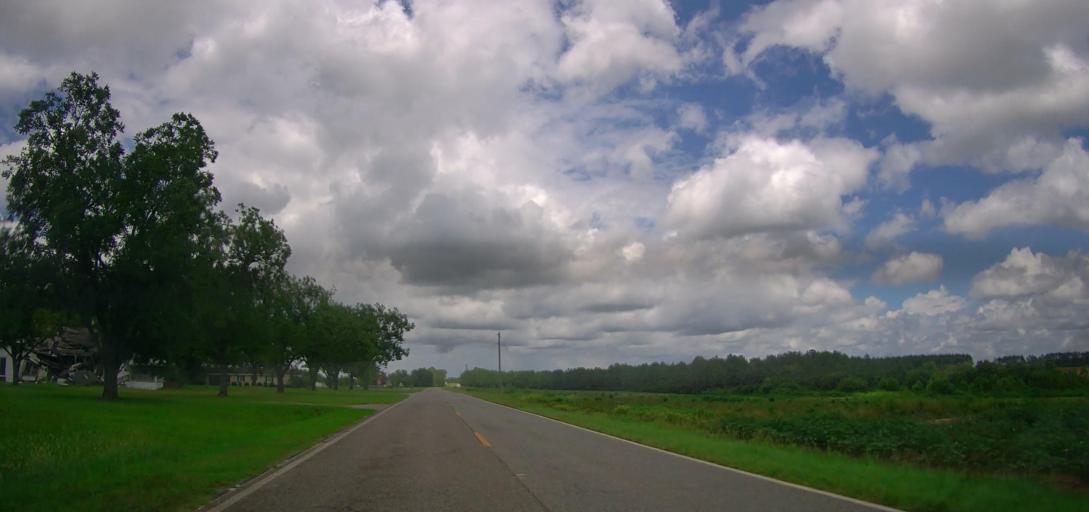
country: US
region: Georgia
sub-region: Wilcox County
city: Rochelle
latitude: 31.8800
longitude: -83.5573
